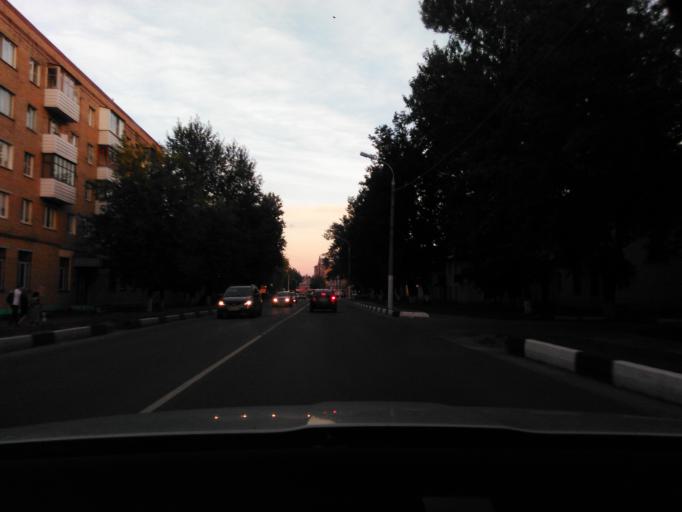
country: RU
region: Moskovskaya
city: Klin
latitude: 56.3261
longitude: 36.7177
